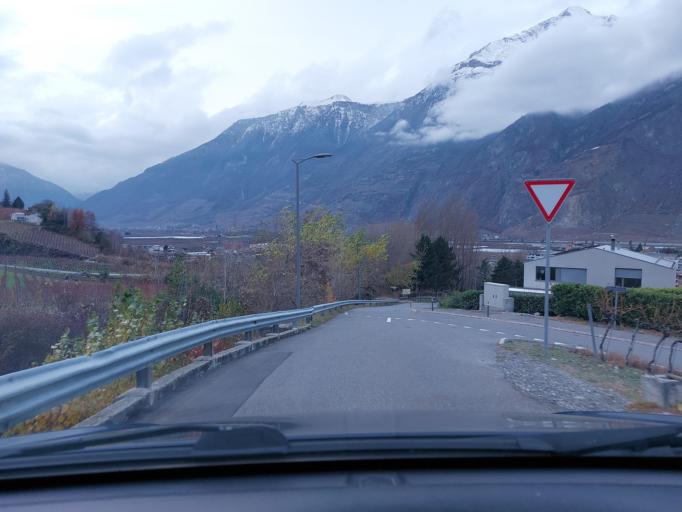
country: CH
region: Valais
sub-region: Martigny District
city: Saxon
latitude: 46.1462
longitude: 7.1776
